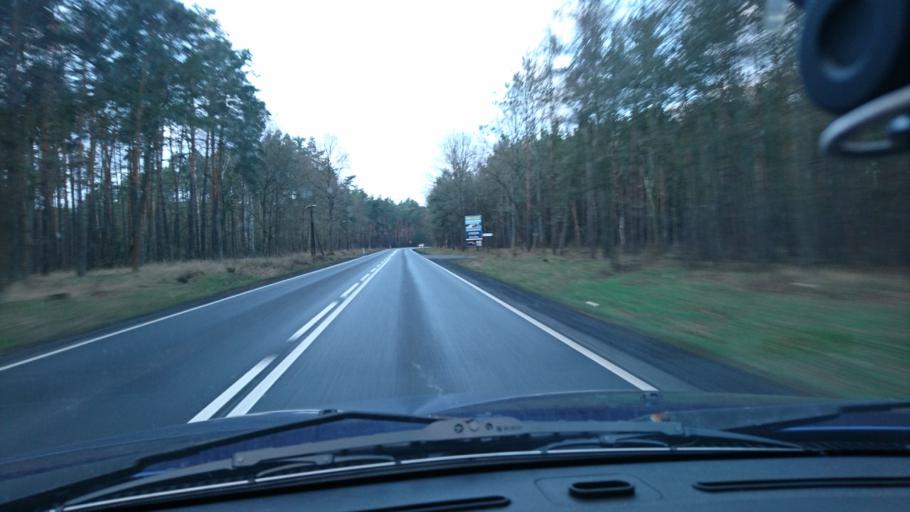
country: PL
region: Greater Poland Voivodeship
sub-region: Powiat kepinski
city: Kepno
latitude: 51.3360
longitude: 17.9549
